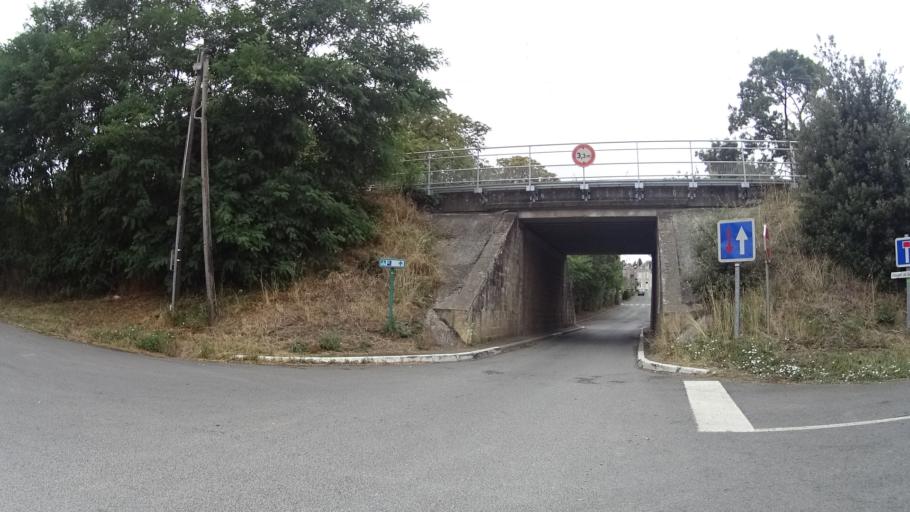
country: FR
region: Pays de la Loire
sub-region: Departement de Maine-et-Loire
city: La Possonniere
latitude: 47.3720
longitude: -0.6846
